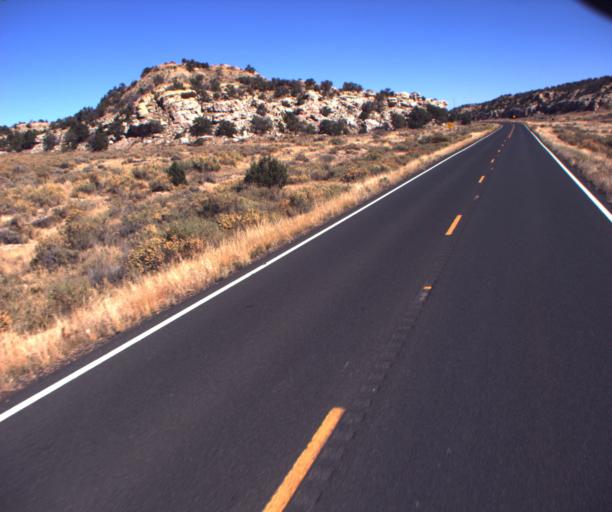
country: US
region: Arizona
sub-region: Apache County
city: Ganado
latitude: 35.7608
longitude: -109.8125
